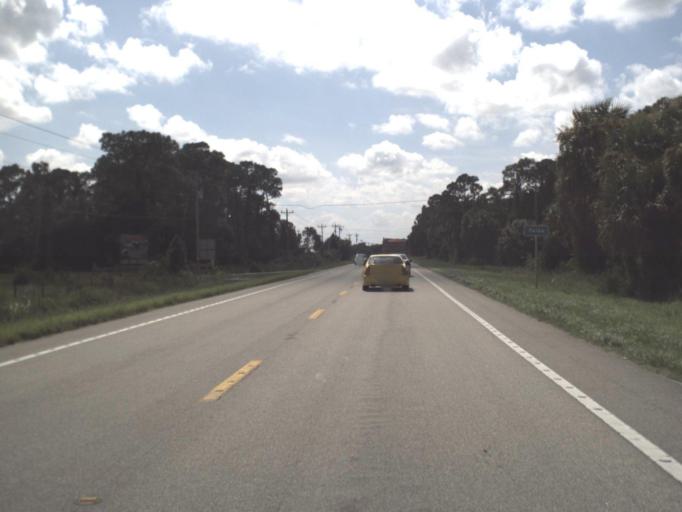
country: US
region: Florida
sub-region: Collier County
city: Immokalee
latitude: 26.5699
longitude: -81.4362
